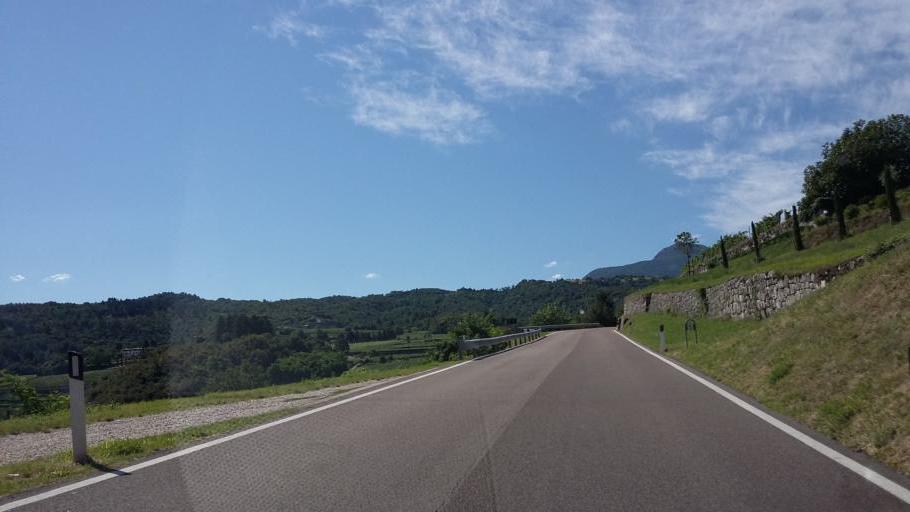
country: IT
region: Trentino-Alto Adige
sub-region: Provincia di Trento
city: Mori
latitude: 45.8441
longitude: 10.9730
